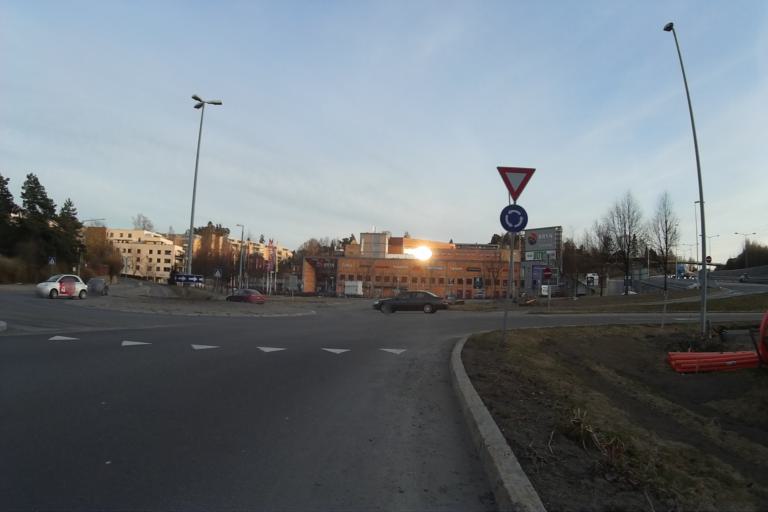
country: NO
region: Oslo
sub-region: Oslo
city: Oslo
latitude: 59.9049
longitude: 10.8216
